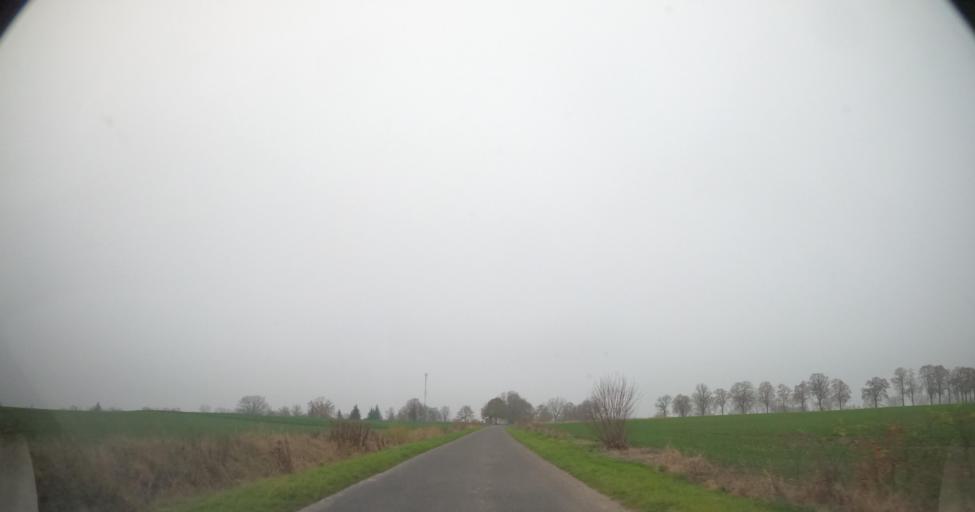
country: PL
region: West Pomeranian Voivodeship
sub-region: Powiat drawski
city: Drawsko Pomorskie
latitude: 53.5923
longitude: 15.7325
